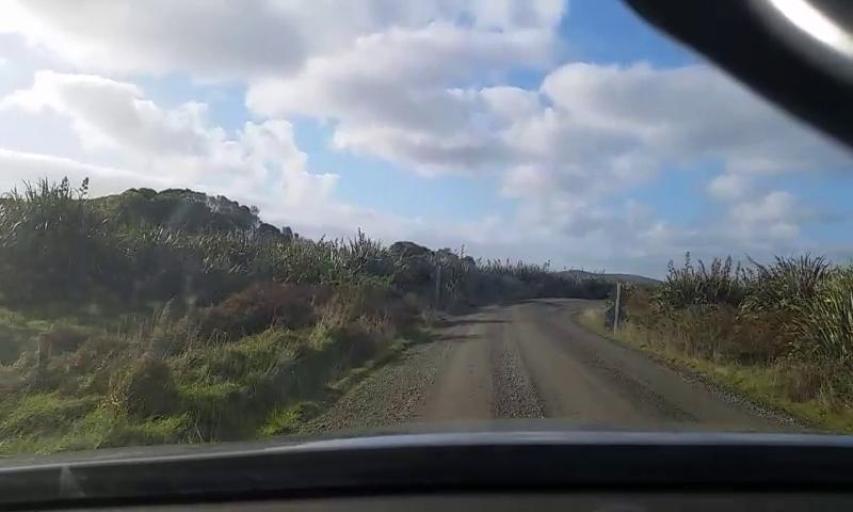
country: NZ
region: Otago
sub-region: Clutha District
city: Papatowai
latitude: -46.6505
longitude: 169.1001
